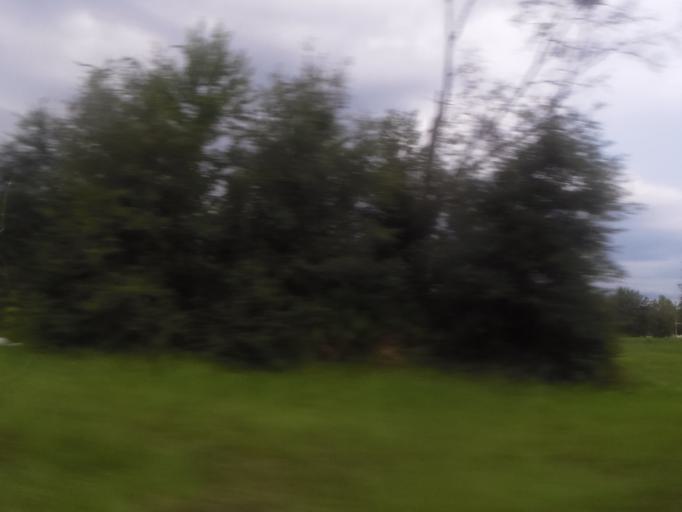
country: US
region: Florida
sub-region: Clay County
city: Bellair-Meadowbrook Terrace
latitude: 30.2841
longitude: -81.8047
